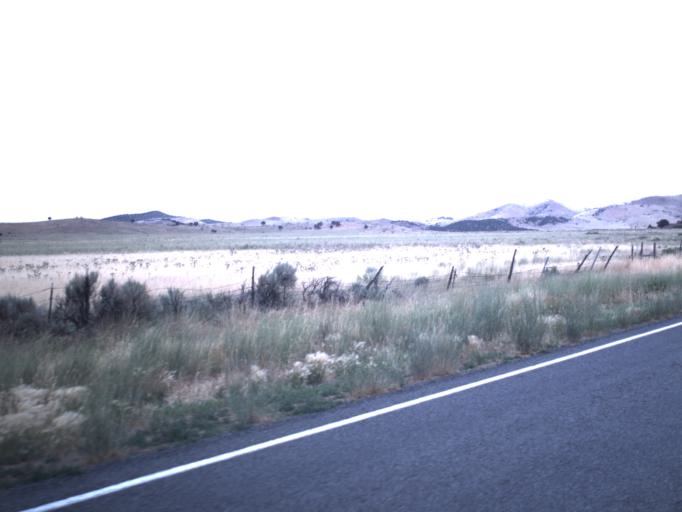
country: US
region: Utah
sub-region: Beaver County
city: Beaver
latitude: 38.5936
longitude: -112.5818
